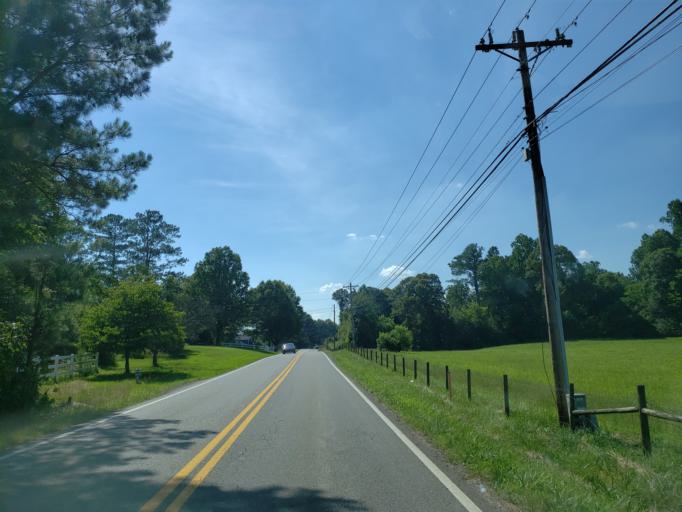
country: US
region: Georgia
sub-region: Cherokee County
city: Woodstock
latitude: 34.1163
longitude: -84.4619
